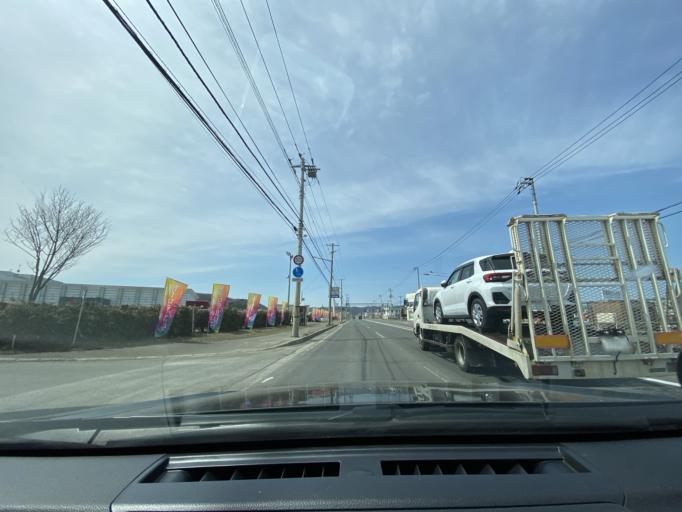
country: JP
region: Hokkaido
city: Kitami
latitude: 43.7978
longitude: 143.8346
